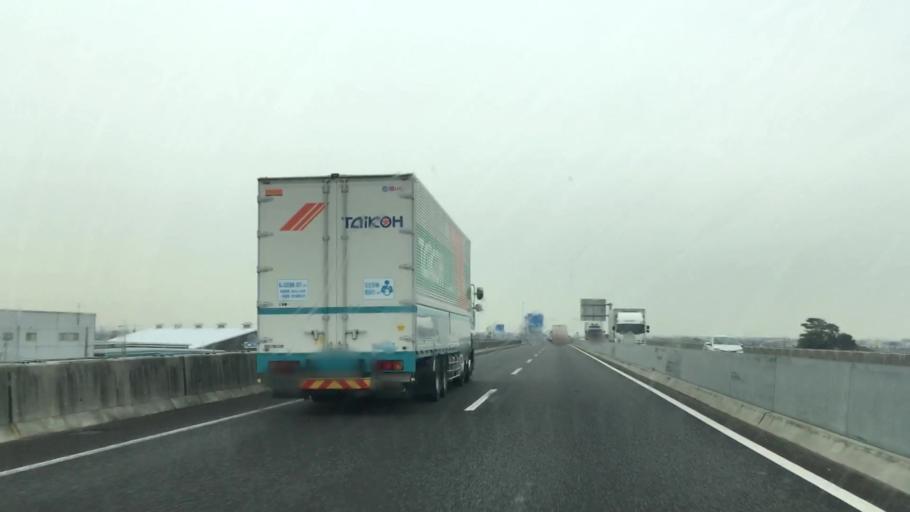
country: JP
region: Aichi
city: Anjo
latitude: 34.9551
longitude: 137.0372
